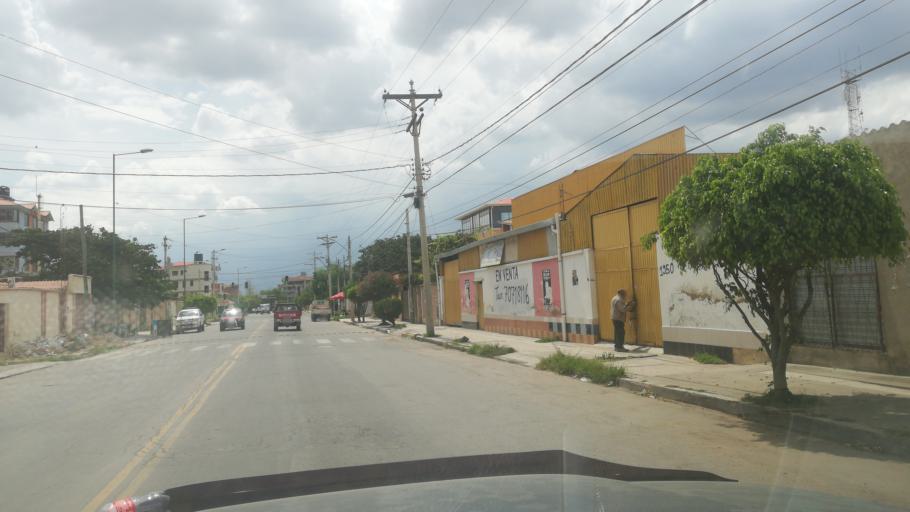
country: BO
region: Cochabamba
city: Cochabamba
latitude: -17.4035
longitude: -66.1774
